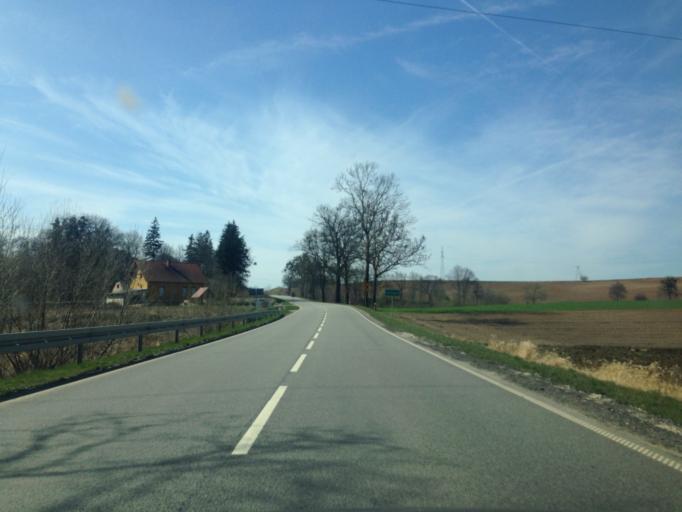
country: PL
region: Pomeranian Voivodeship
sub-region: Powiat starogardzki
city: Smetowo Graniczne
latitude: 53.7390
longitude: 18.7075
